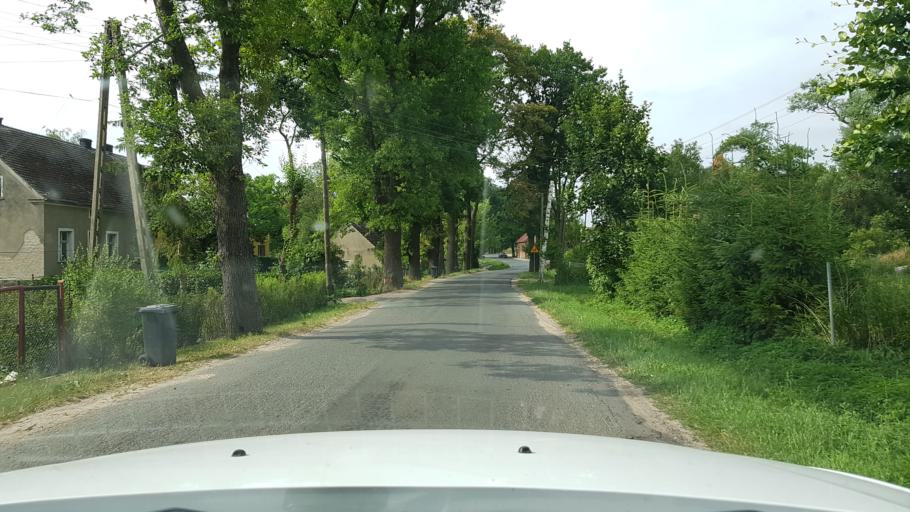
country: PL
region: West Pomeranian Voivodeship
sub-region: Powiat gryfinski
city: Moryn
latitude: 52.8976
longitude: 14.3761
